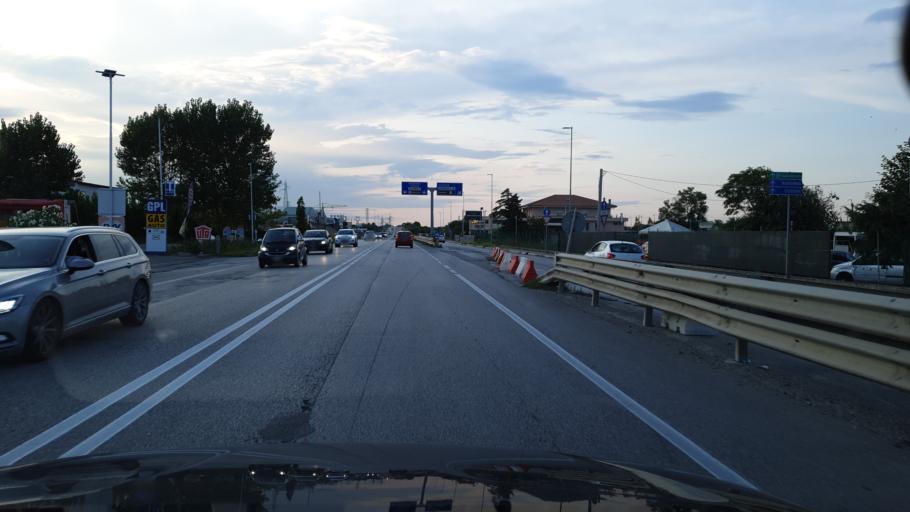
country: IT
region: Emilia-Romagna
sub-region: Forli-Cesena
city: Cesenatico
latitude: 44.1932
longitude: 12.3977
